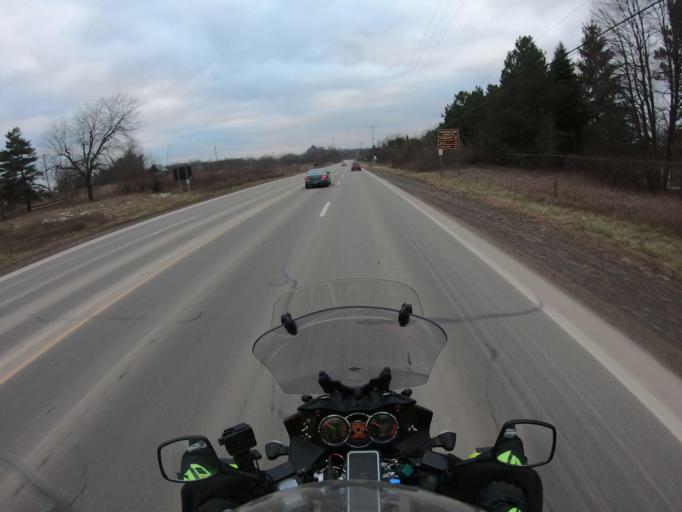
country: US
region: Michigan
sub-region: Oakland County
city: Holly
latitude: 42.8172
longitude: -83.5493
